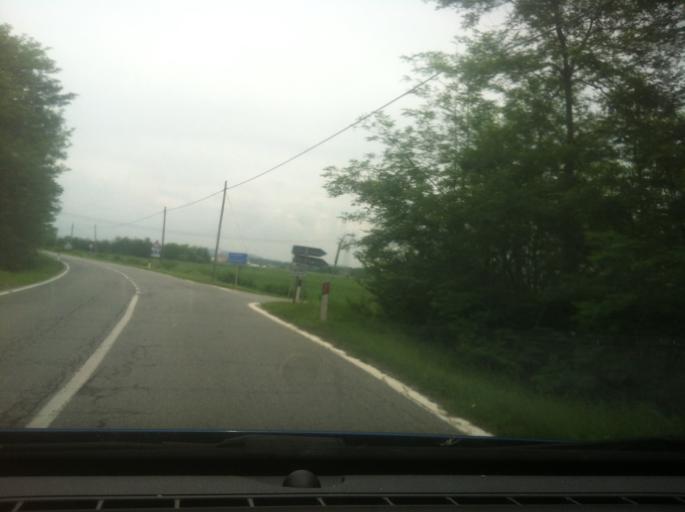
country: IT
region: Piedmont
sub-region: Provincia di Torino
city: Foglizzo
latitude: 45.2490
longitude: 7.8096
